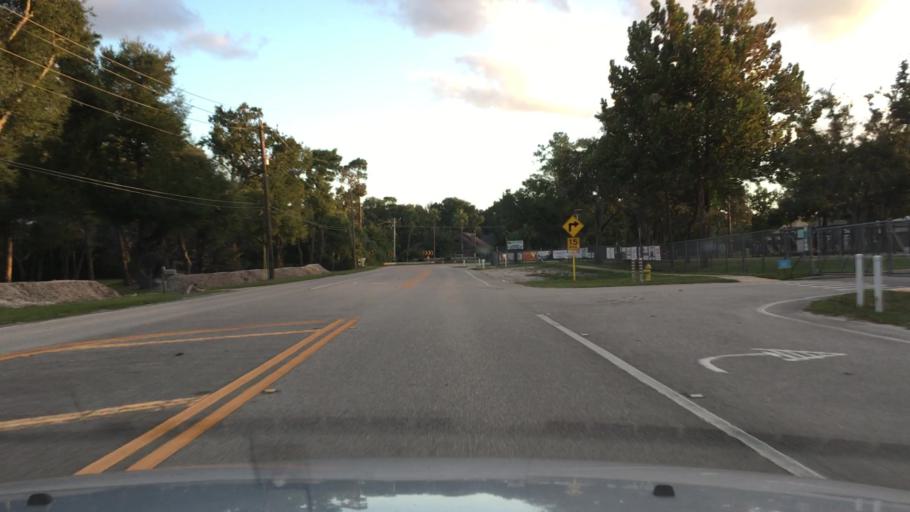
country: US
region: Florida
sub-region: Volusia County
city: Ormond Beach
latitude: 29.2758
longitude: -81.1130
